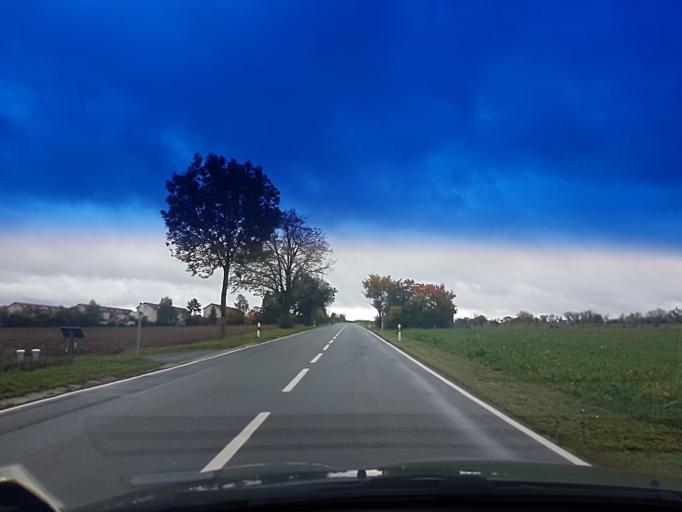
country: DE
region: Bavaria
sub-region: Upper Franconia
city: Bindlach
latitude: 49.9994
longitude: 11.6237
